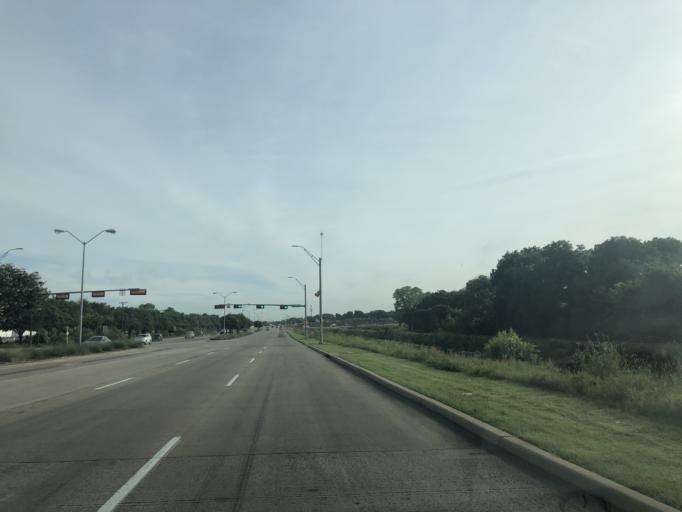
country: US
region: Texas
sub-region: Dallas County
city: Irving
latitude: 32.7976
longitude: -96.9944
